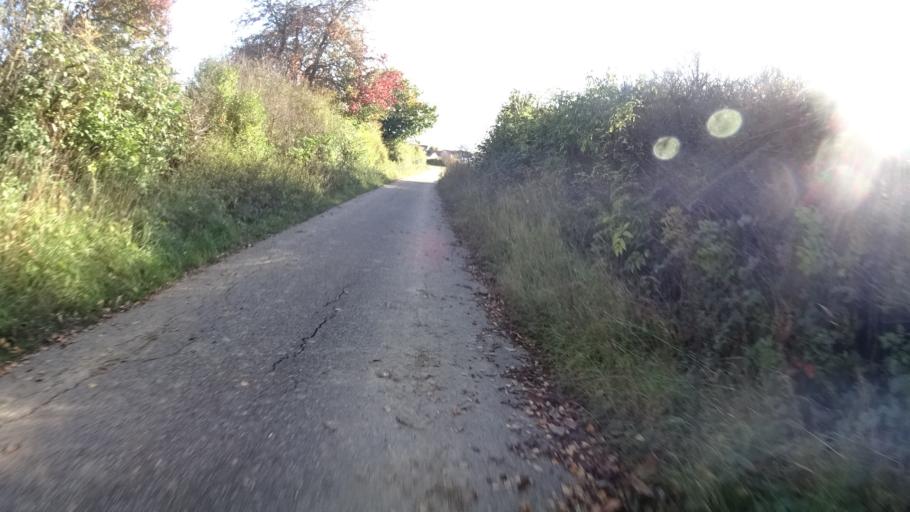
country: DE
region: Bavaria
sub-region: Upper Bavaria
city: Bohmfeld
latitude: 48.8413
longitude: 11.3619
